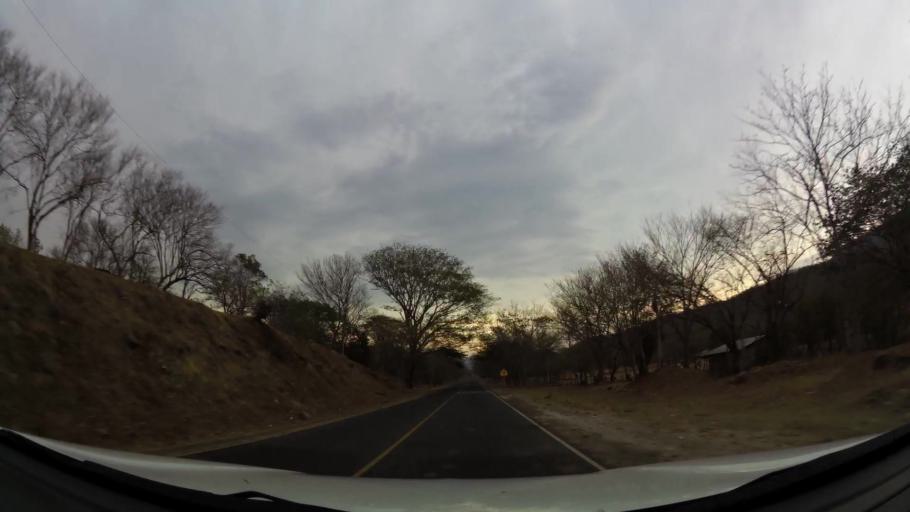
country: NI
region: Leon
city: La Jicaral
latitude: 12.6975
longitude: -86.4038
